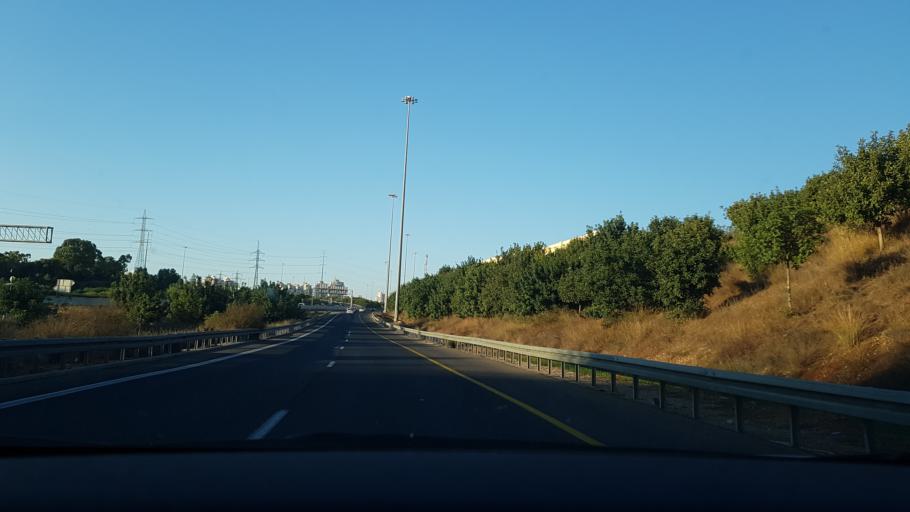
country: IL
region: Central District
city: Rishon LeZiyyon
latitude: 31.9562
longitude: 34.7858
